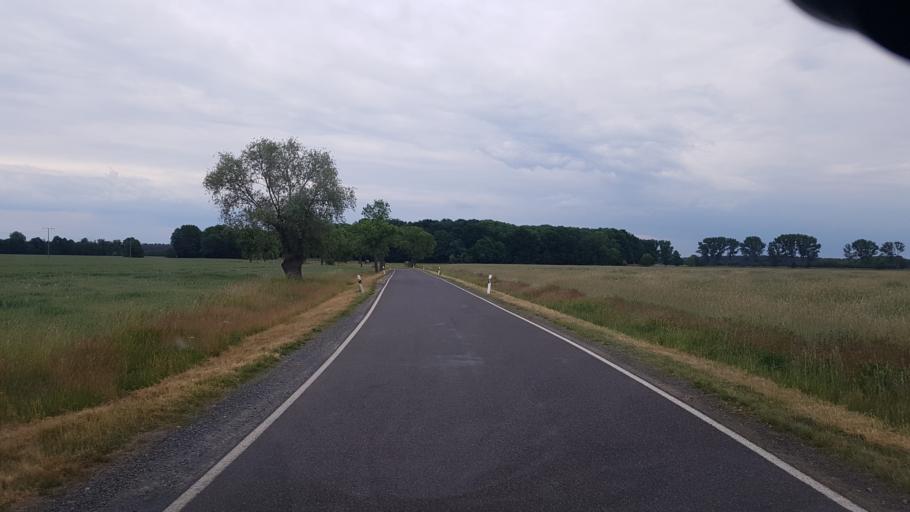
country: DE
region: Saxony-Anhalt
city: Holzdorf
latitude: 51.8057
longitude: 13.2312
